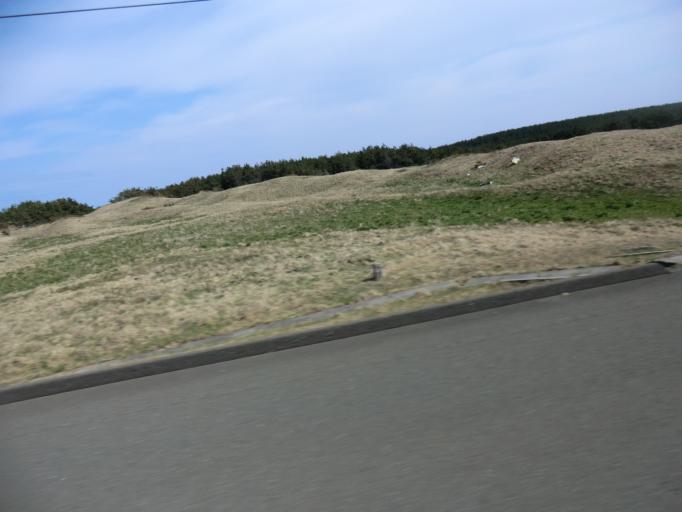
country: JP
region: Aomori
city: Mutsu
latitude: 41.4259
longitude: 141.4584
